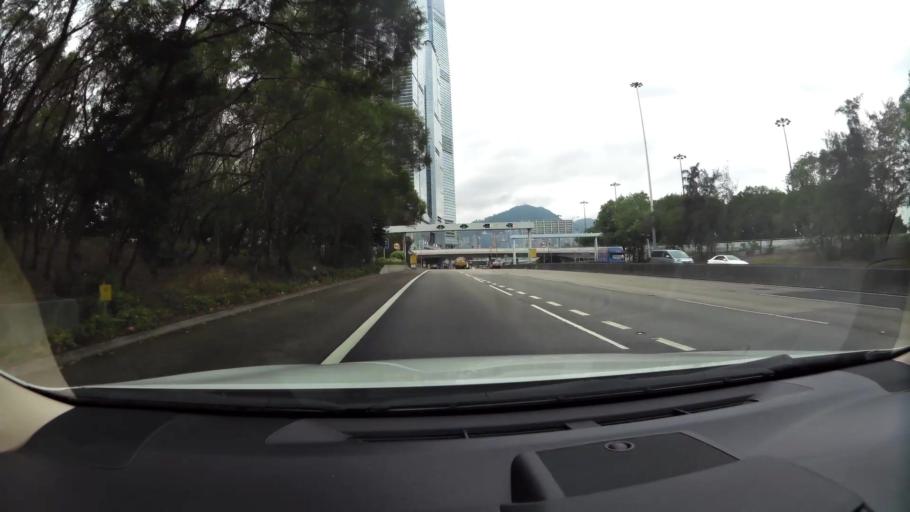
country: HK
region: Sham Shui Po
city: Sham Shui Po
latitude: 22.3093
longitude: 114.1616
